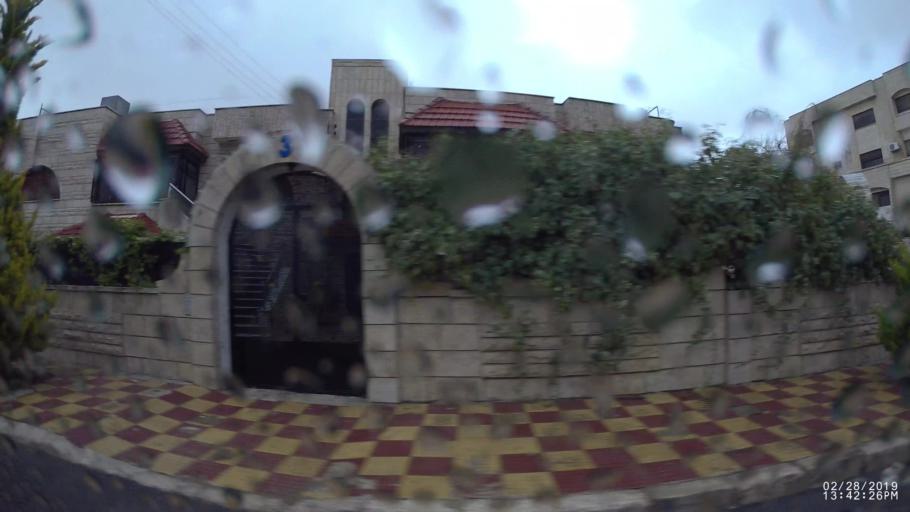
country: JO
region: Amman
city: Al Jubayhah
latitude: 32.0263
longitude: 35.8749
